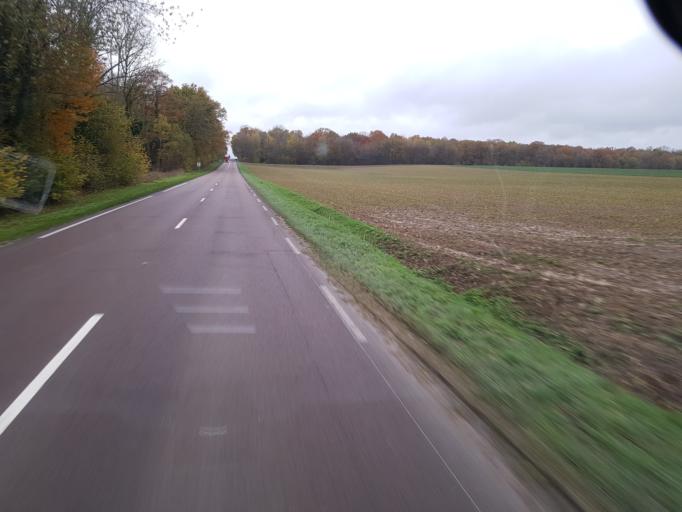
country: FR
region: Champagne-Ardenne
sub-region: Departement de la Marne
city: Esternay
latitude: 48.7946
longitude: 3.6256
